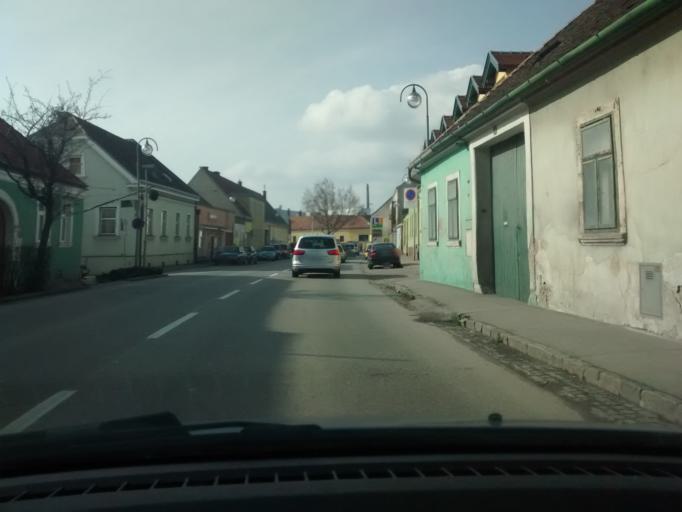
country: AT
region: Lower Austria
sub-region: Politischer Bezirk Baden
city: Traiskirchen
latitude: 48.0161
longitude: 16.2934
